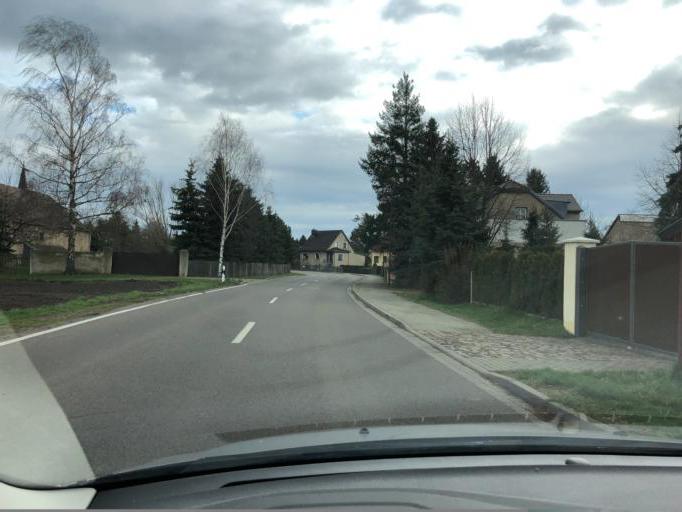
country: DE
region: Saxony
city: Markranstadt
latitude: 51.2762
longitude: 12.2051
